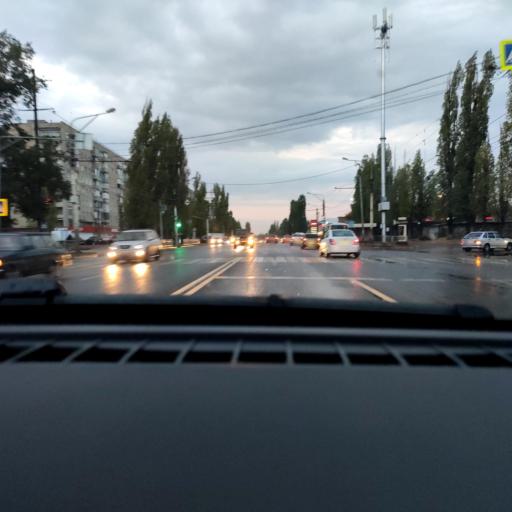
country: RU
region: Voronezj
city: Maslovka
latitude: 51.6094
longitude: 39.2373
